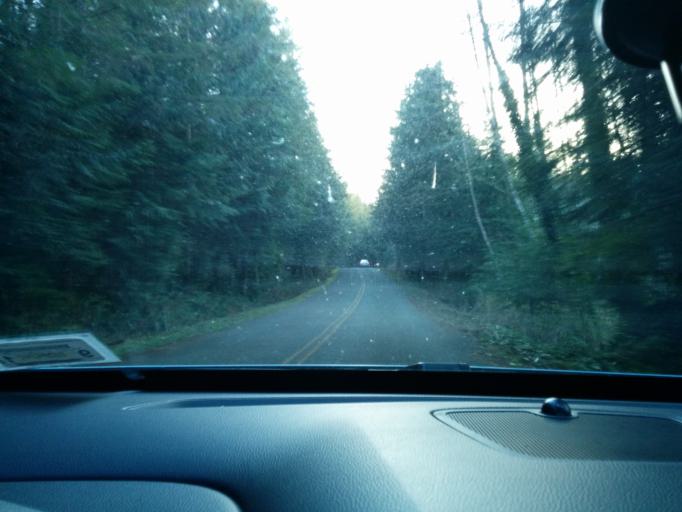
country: US
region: Washington
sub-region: Snohomish County
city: Sultan
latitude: 47.9005
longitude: -121.7655
